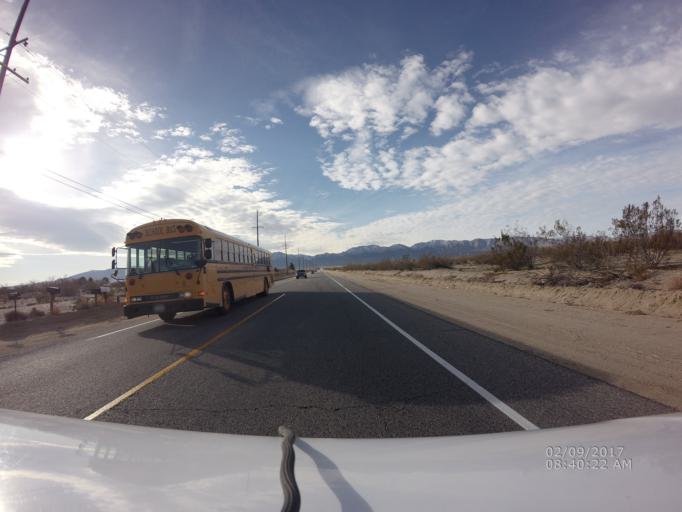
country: US
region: California
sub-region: Los Angeles County
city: Lake Los Angeles
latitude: 34.5387
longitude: -117.8356
